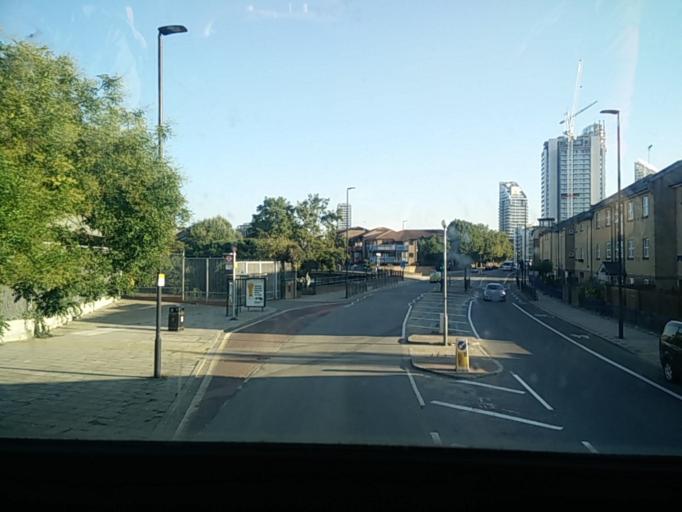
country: GB
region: England
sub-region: Greater London
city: Poplar
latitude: 51.5018
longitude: -0.0088
